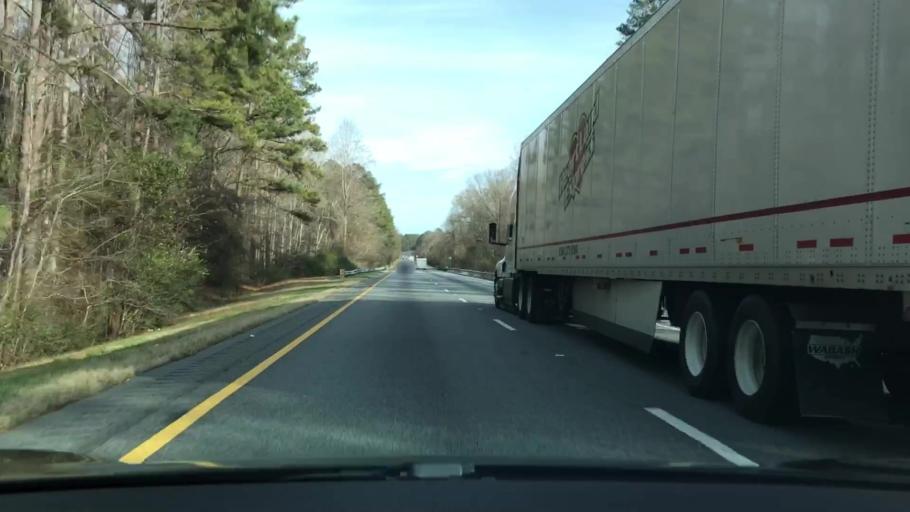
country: US
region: Georgia
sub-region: Morgan County
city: Madison
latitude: 33.5765
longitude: -83.5530
